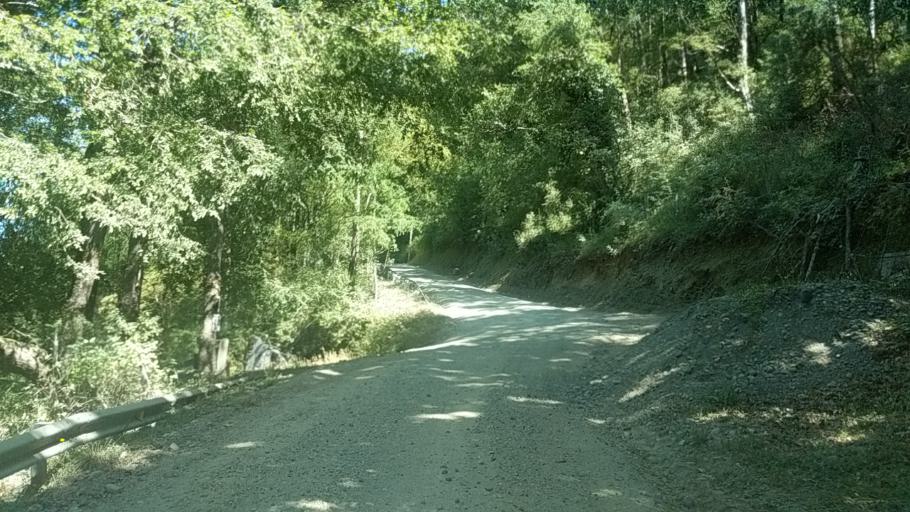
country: CL
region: Araucania
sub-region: Provincia de Cautin
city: Pucon
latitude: -39.0634
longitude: -71.7165
